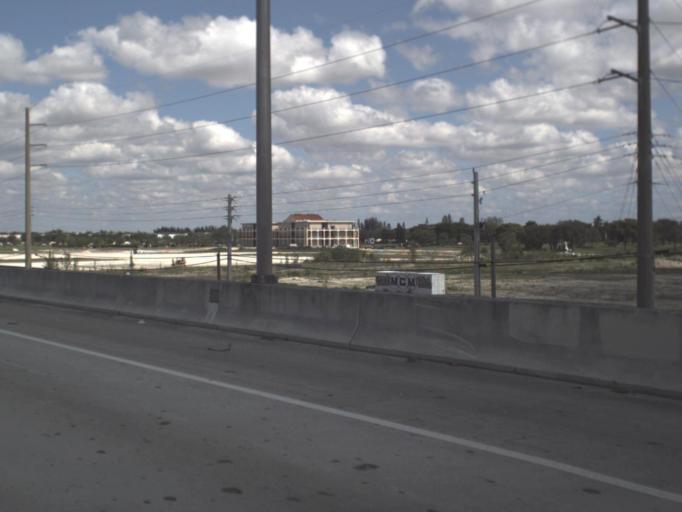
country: US
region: Florida
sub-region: Miami-Dade County
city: Sweetwater
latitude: 25.7970
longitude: -80.3858
